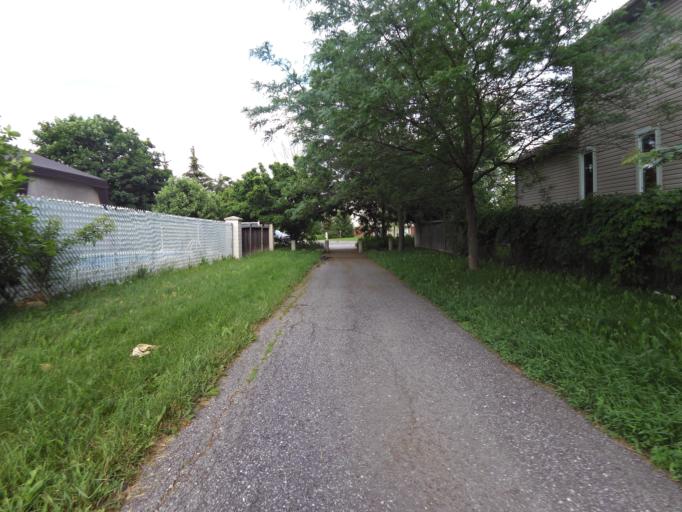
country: CA
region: Ontario
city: Bells Corners
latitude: 45.2825
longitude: -75.7144
